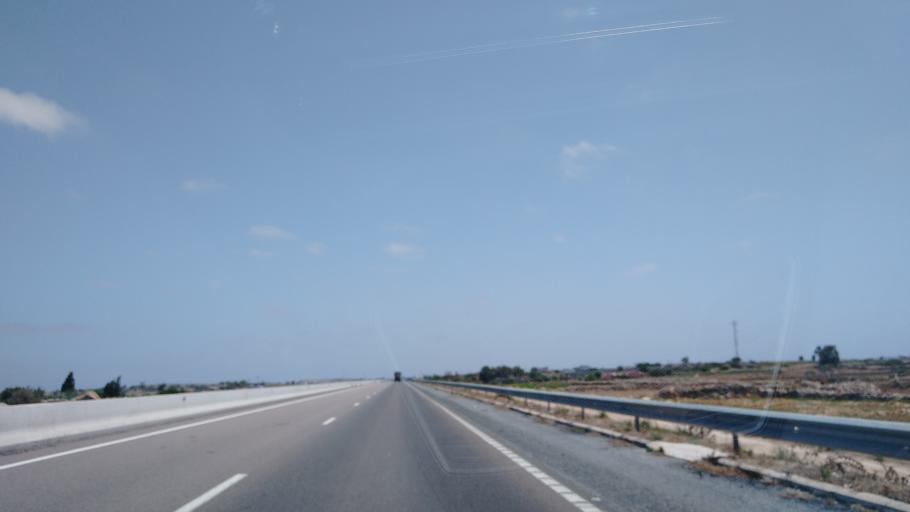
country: MA
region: Doukkala-Abda
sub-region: El-Jadida
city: El Jadida
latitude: 33.2198
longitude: -8.4386
